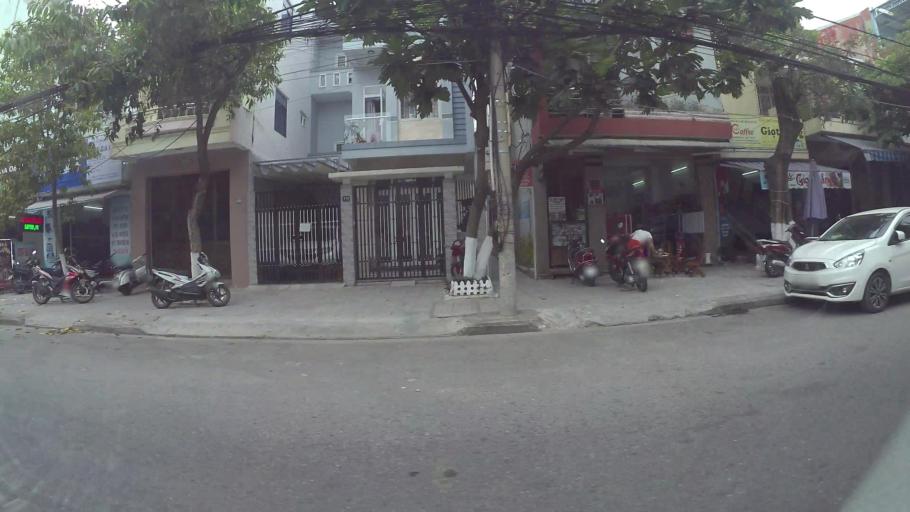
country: VN
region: Da Nang
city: Da Nang
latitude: 16.0506
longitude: 108.2132
